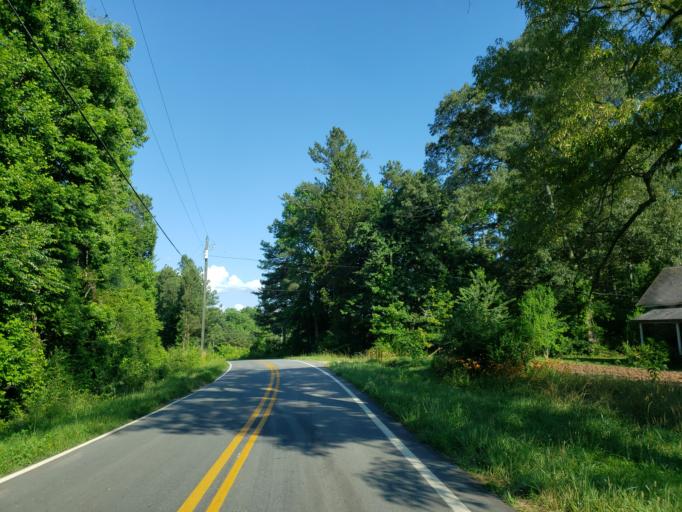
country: US
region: Georgia
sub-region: Haralson County
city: Bremen
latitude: 33.7045
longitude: -85.1082
